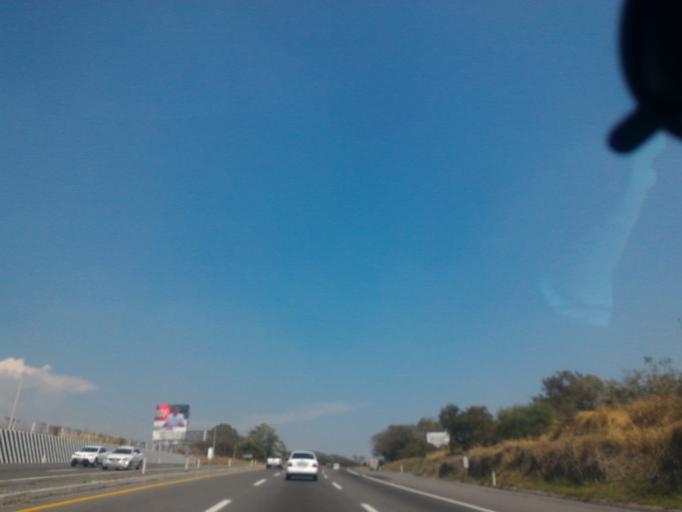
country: MX
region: Colima
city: Cuauhtemoc
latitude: 19.2924
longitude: -103.6501
